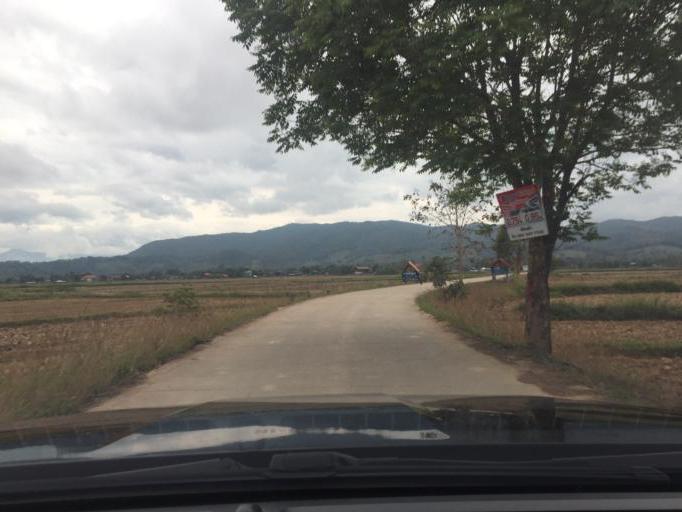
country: TH
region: Phayao
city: Pong
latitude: 19.1653
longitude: 100.3151
